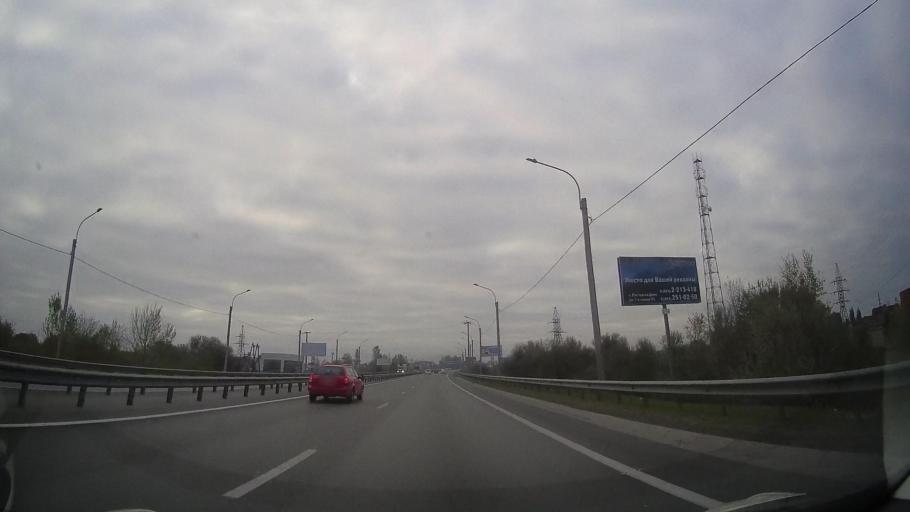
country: RU
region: Rostov
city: Bataysk
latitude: 47.1591
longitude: 39.7657
